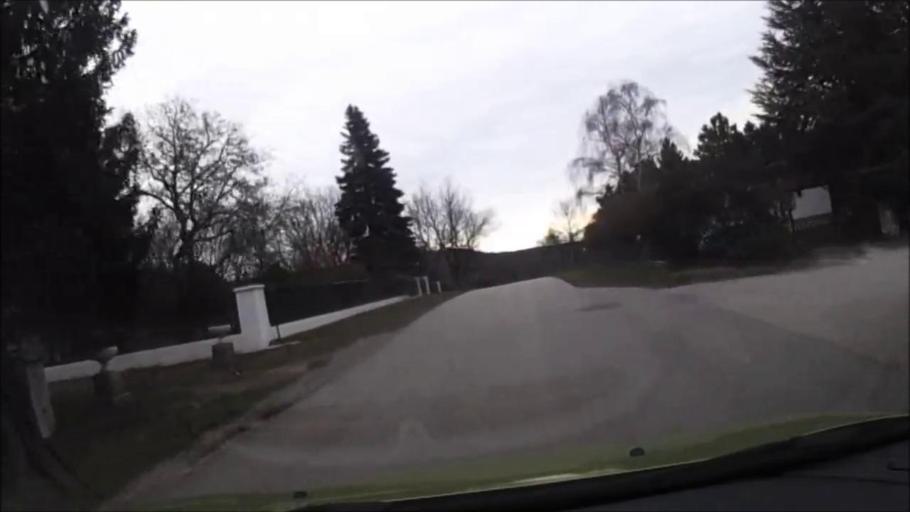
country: AT
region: Burgenland
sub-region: Eisenstadt-Umgebung
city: Loretto
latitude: 47.8994
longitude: 16.5222
